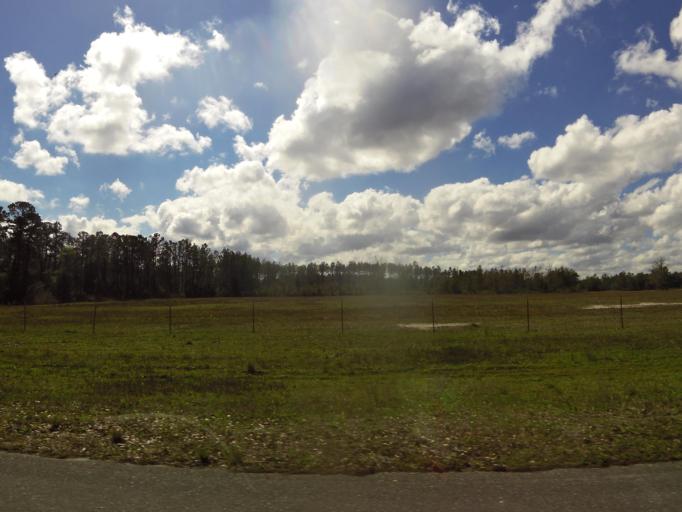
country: US
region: Florida
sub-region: Clay County
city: Green Cove Springs
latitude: 29.8680
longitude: -81.6973
